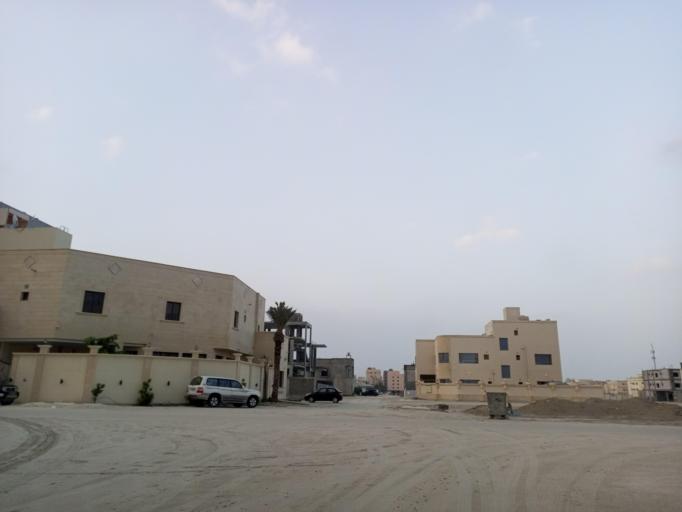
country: BH
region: Muharraq
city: Al Hadd
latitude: 26.2349
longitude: 50.6468
